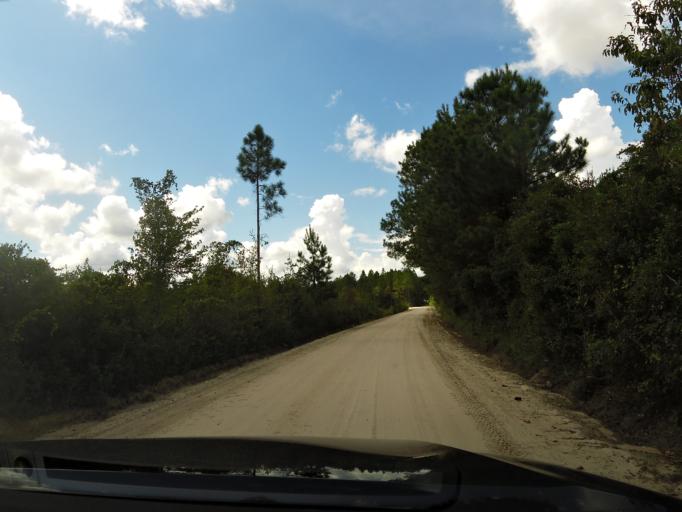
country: US
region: Georgia
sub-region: Brantley County
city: Nahunta
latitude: 31.0933
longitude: -82.0107
